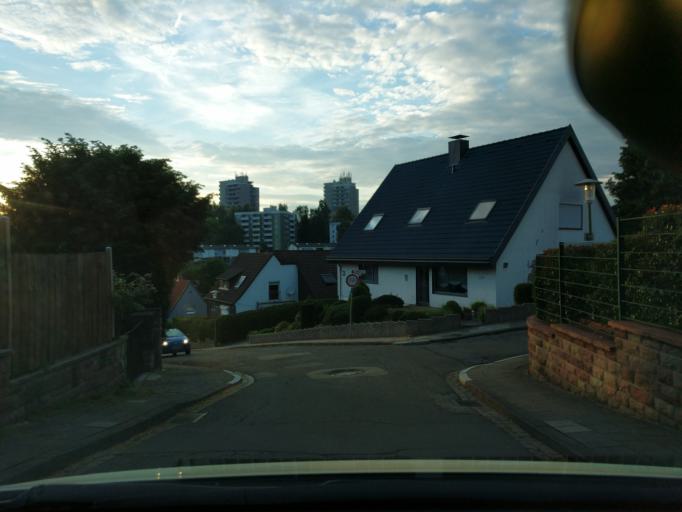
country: DE
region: Rheinland-Pfalz
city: Kaiserslautern
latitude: 49.4464
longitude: 7.7417
